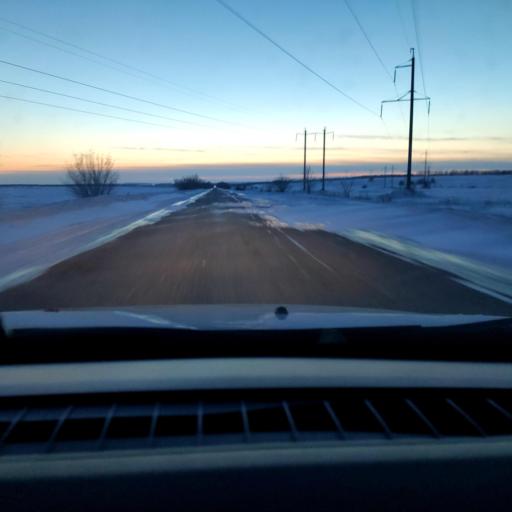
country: RU
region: Samara
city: Georgiyevka
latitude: 53.3403
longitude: 50.9659
